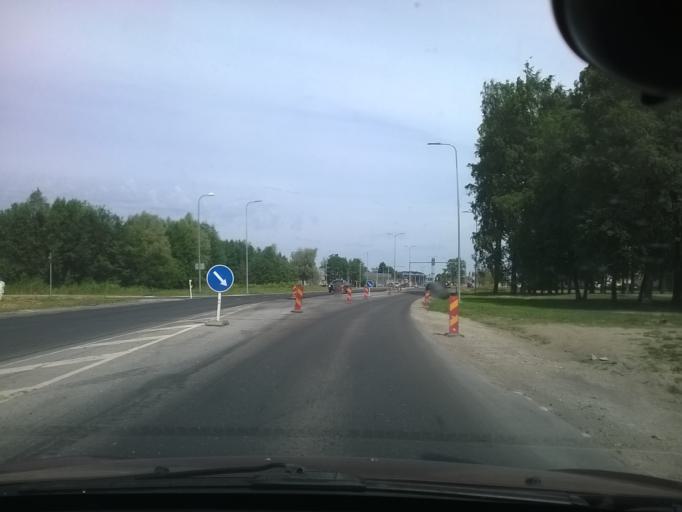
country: EE
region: Harju
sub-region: Saue vald
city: Laagri
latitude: 59.4189
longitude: 24.6382
